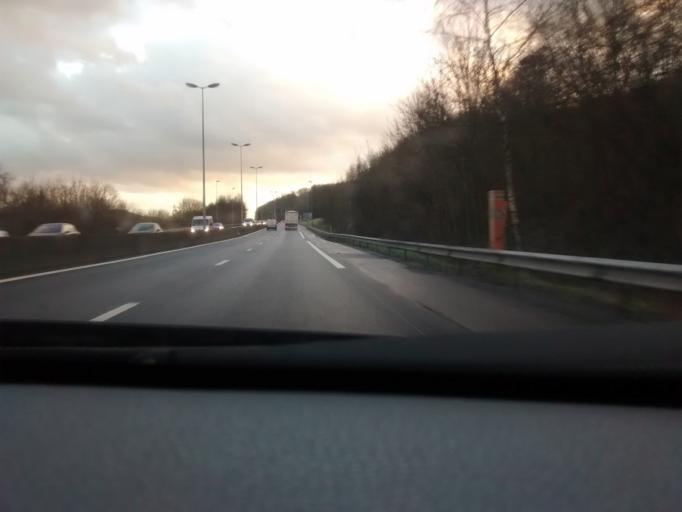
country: FR
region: Haute-Normandie
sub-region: Departement de la Seine-Maritime
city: Darnetal
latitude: 49.4569
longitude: 1.1440
